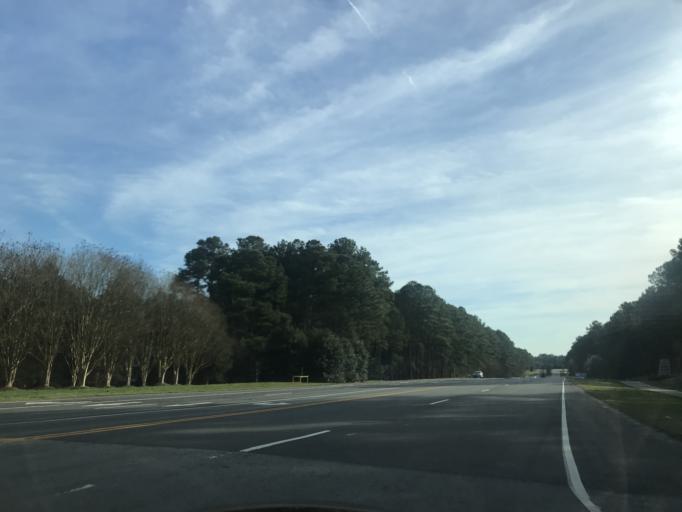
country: US
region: North Carolina
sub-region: Wake County
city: Morrisville
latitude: 35.9034
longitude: -78.8580
